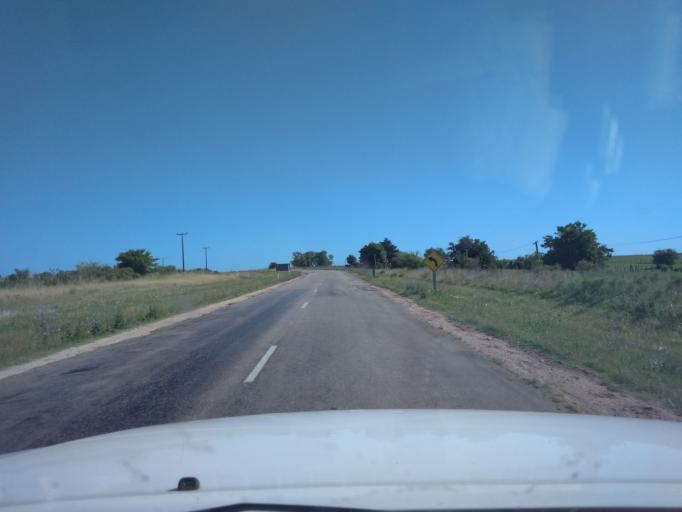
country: UY
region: Canelones
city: San Ramon
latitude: -34.2137
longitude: -55.9293
